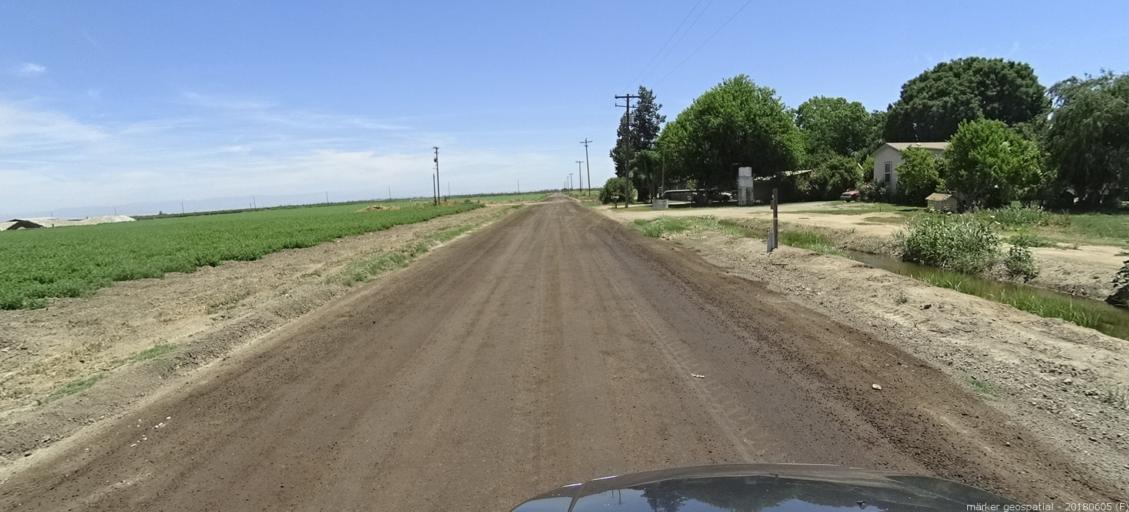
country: US
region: California
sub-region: Madera County
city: Chowchilla
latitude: 37.1055
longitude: -120.3188
